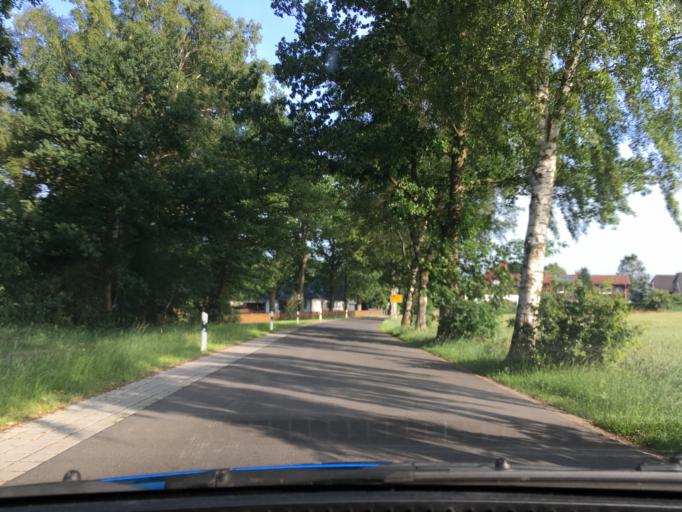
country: DE
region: Lower Saxony
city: Kakenstorf
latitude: 53.3094
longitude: 9.7757
